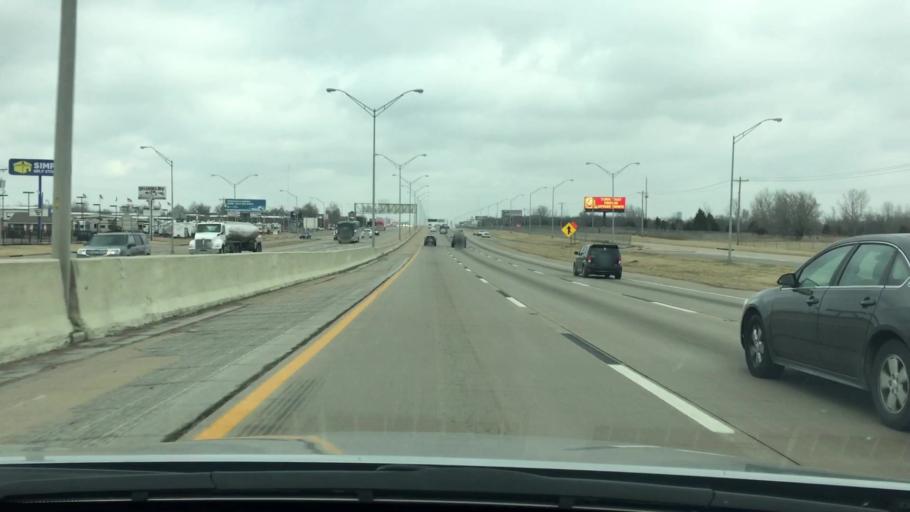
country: US
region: Oklahoma
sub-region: Cleveland County
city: Moore
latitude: 35.3650
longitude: -97.4948
